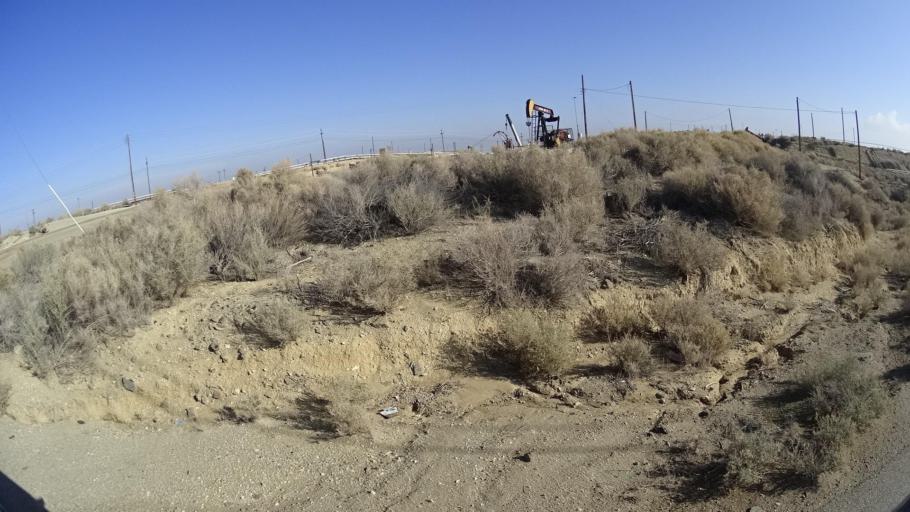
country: US
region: California
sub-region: Kern County
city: Taft Heights
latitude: 35.2224
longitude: -119.6101
